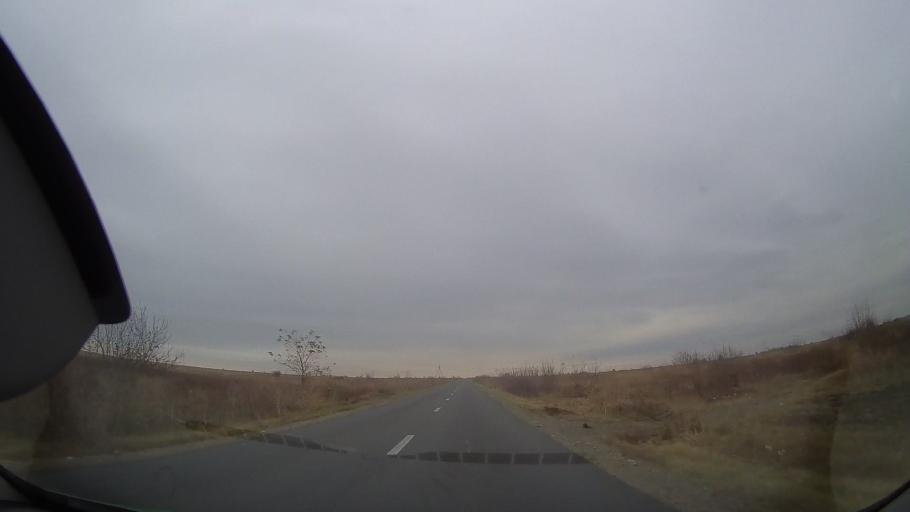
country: RO
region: Ialomita
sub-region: Oras Amara
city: Amara
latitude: 44.6312
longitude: 27.3011
